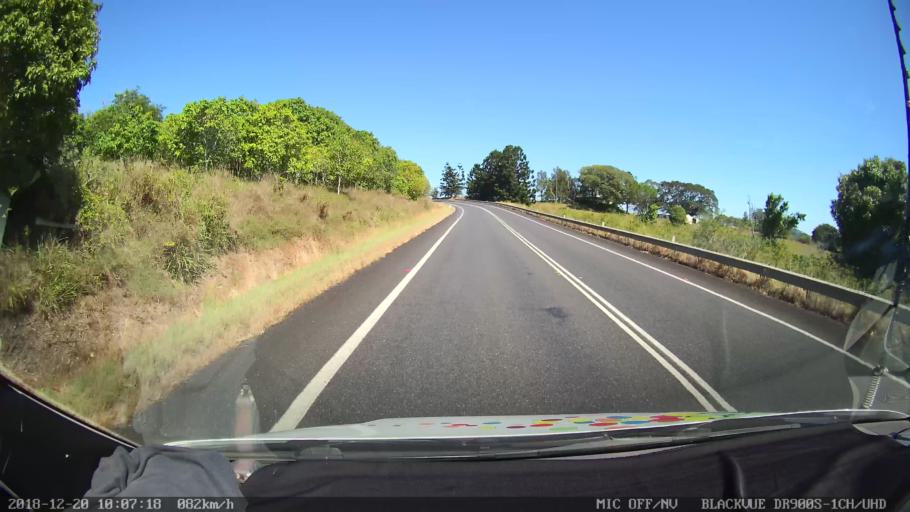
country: AU
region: New South Wales
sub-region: Lismore Municipality
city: Lismore
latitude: -28.8843
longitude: 153.2142
